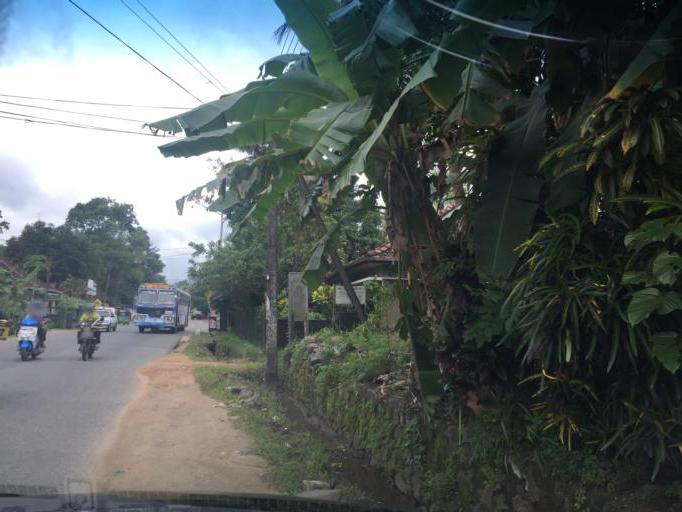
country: LK
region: Western
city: Horana South
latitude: 6.7066
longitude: 80.0687
